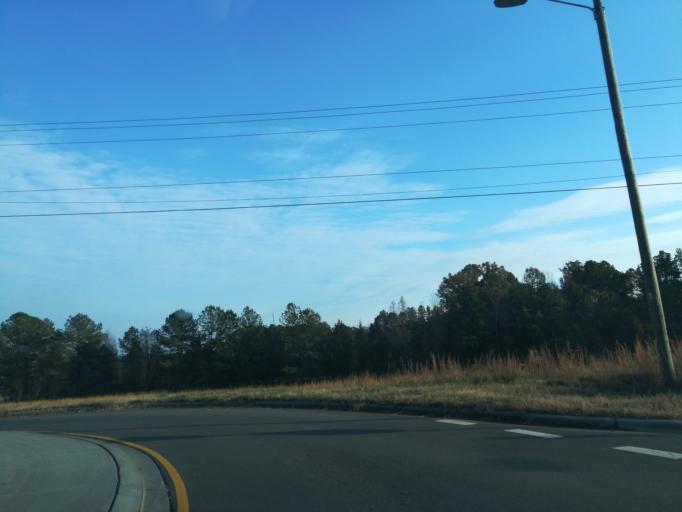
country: US
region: North Carolina
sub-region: Orange County
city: Chapel Hill
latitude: 35.9685
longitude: -79.0080
